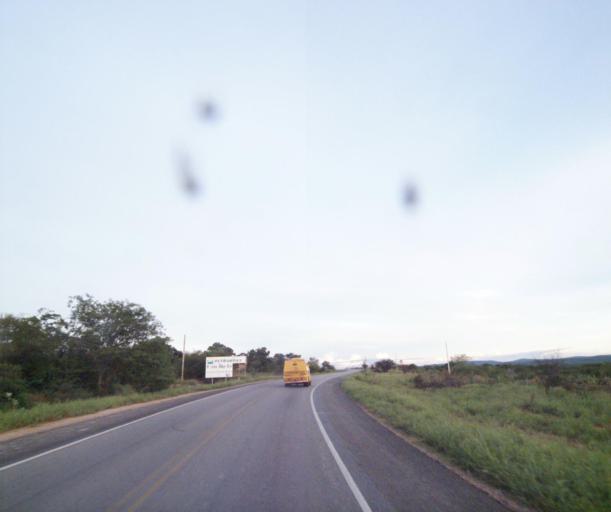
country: BR
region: Bahia
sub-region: Brumado
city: Brumado
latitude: -14.2531
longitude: -41.7422
